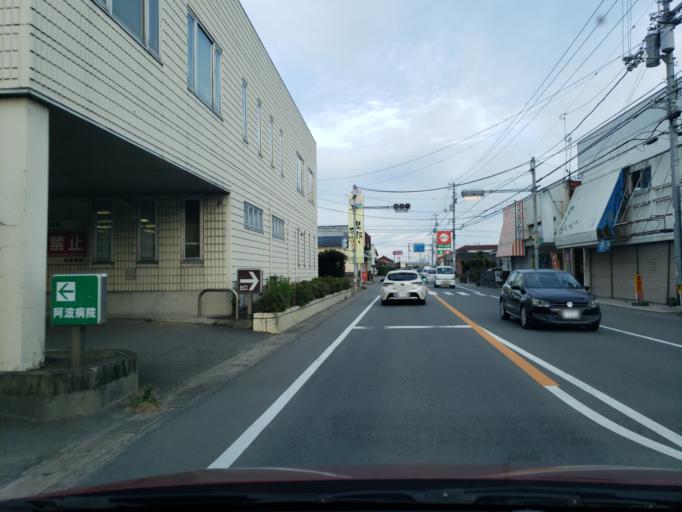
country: JP
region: Tokushima
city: Kamojimacho-jogejima
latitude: 34.0838
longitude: 134.2756
